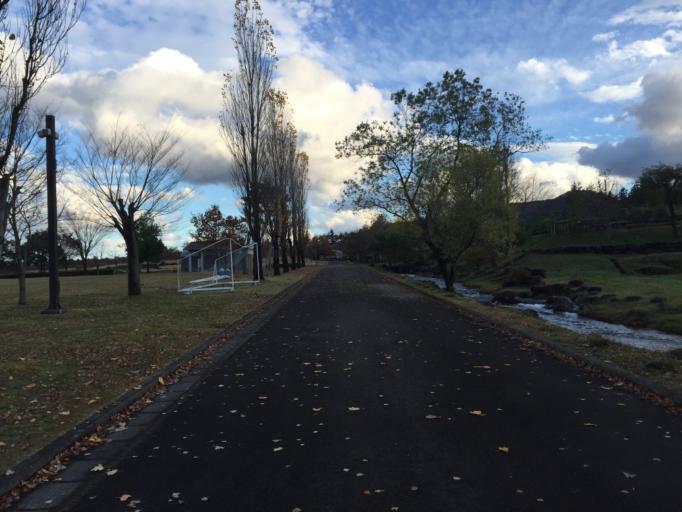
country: JP
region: Fukushima
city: Fukushima-shi
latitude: 37.7166
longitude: 140.3544
